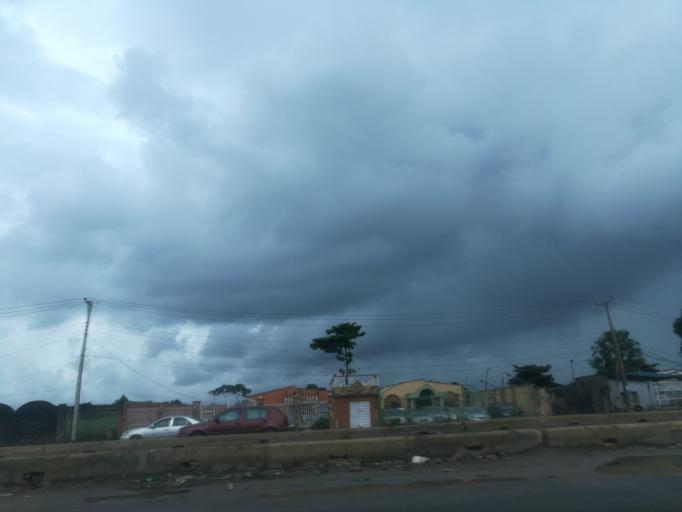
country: NG
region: Lagos
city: Ikeja
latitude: 6.6016
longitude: 3.3333
